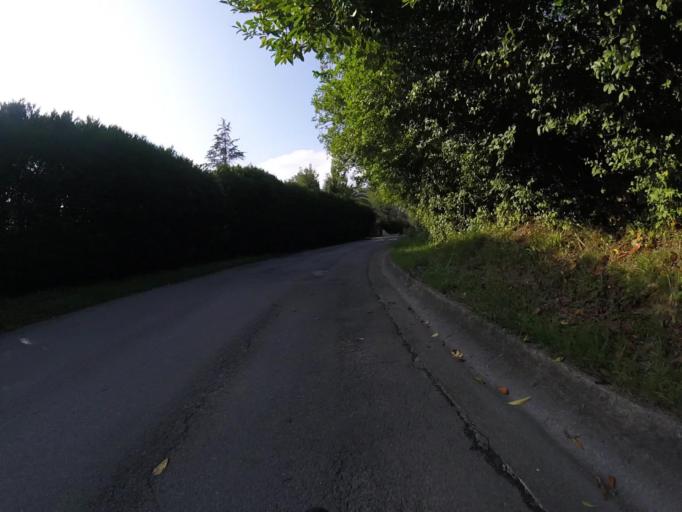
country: ES
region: Basque Country
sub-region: Provincia de Guipuzcoa
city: Irun
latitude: 43.3365
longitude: -1.8336
